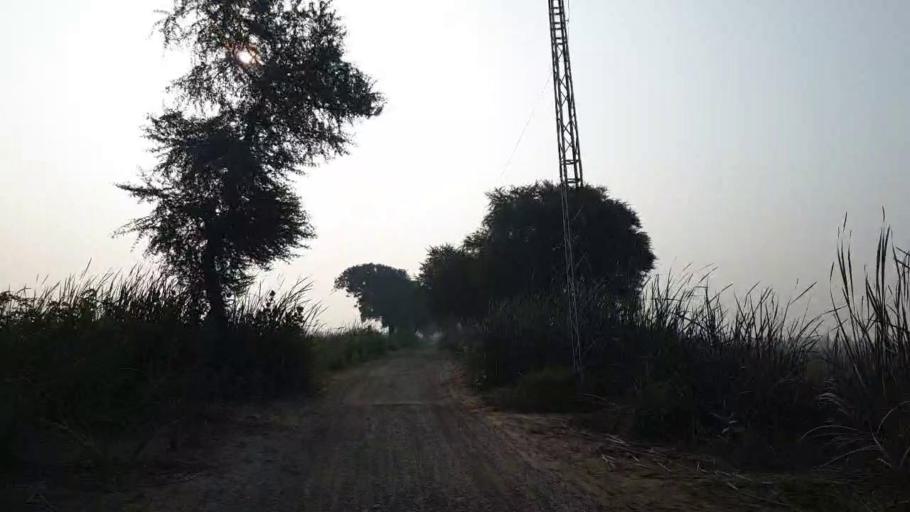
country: PK
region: Sindh
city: Tando Muhammad Khan
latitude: 25.1244
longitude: 68.5615
